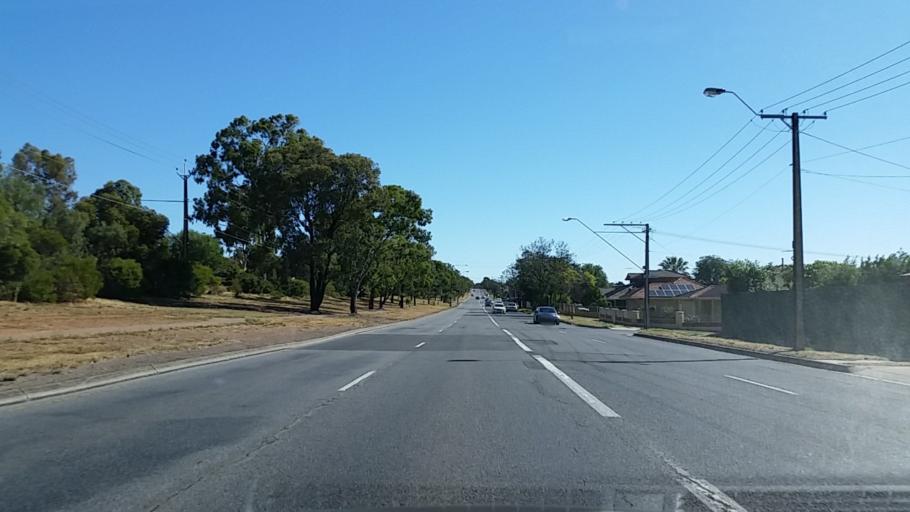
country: AU
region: South Australia
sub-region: Salisbury
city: Ingle Farm
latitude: -34.8260
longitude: 138.6341
